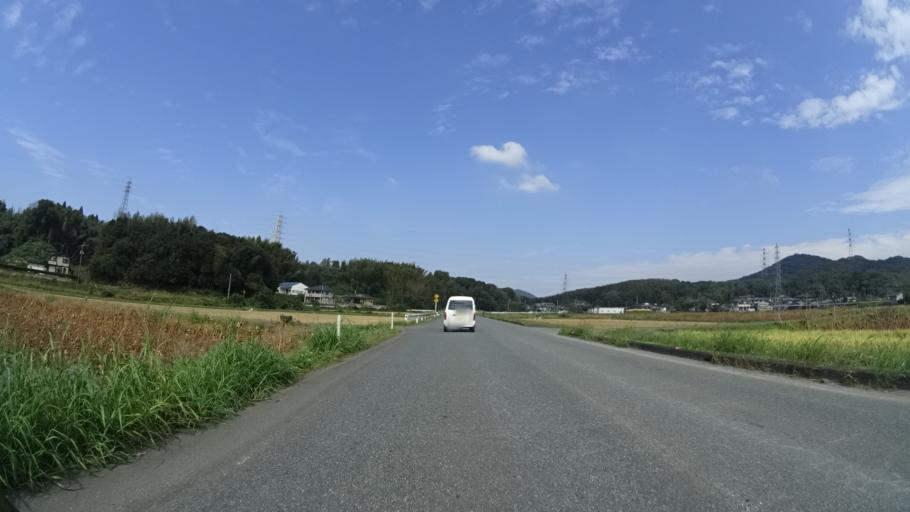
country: JP
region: Kumamoto
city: Matsubase
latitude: 32.6538
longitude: 130.7160
